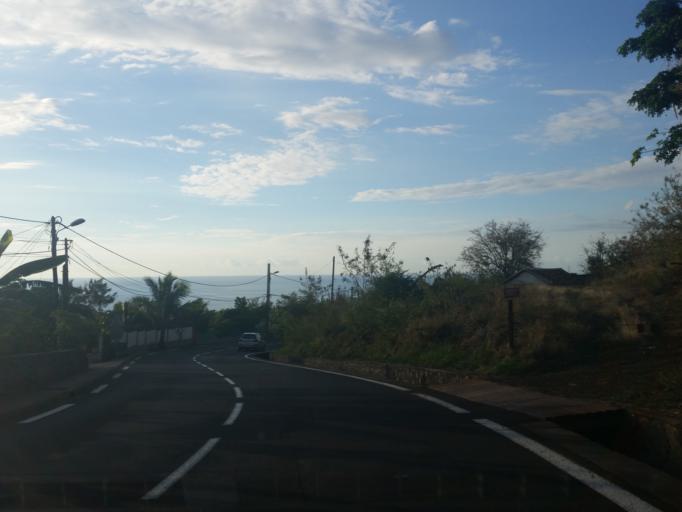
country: RE
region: Reunion
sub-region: Reunion
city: Saint-Leu
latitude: -21.1413
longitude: 55.2838
